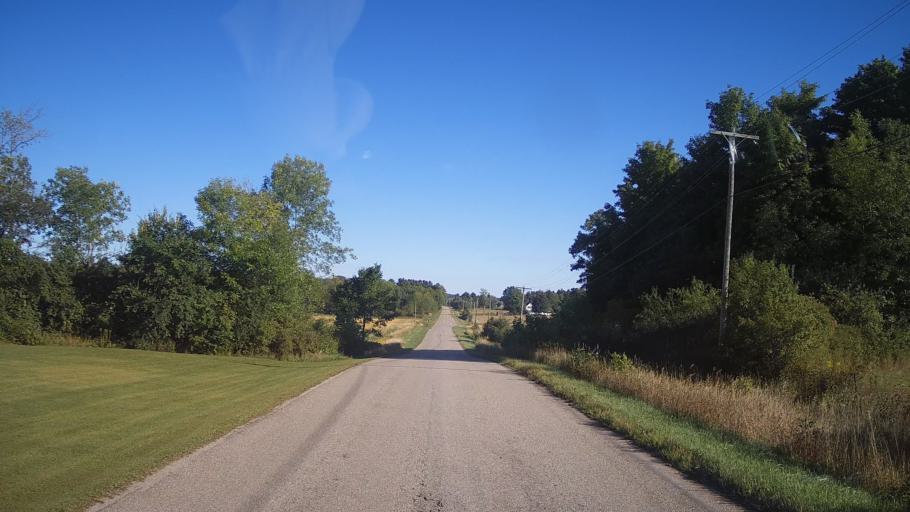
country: US
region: New York
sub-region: Jefferson County
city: Alexandria Bay
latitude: 44.4551
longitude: -75.9863
